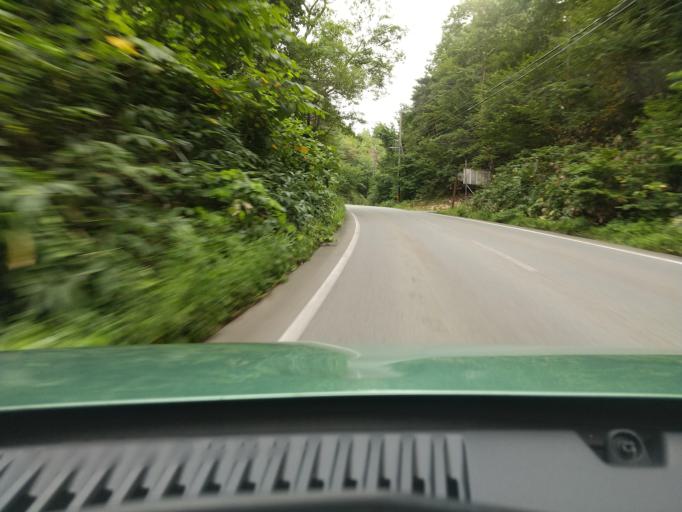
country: JP
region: Akita
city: Akita
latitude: 39.7738
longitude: 140.1336
